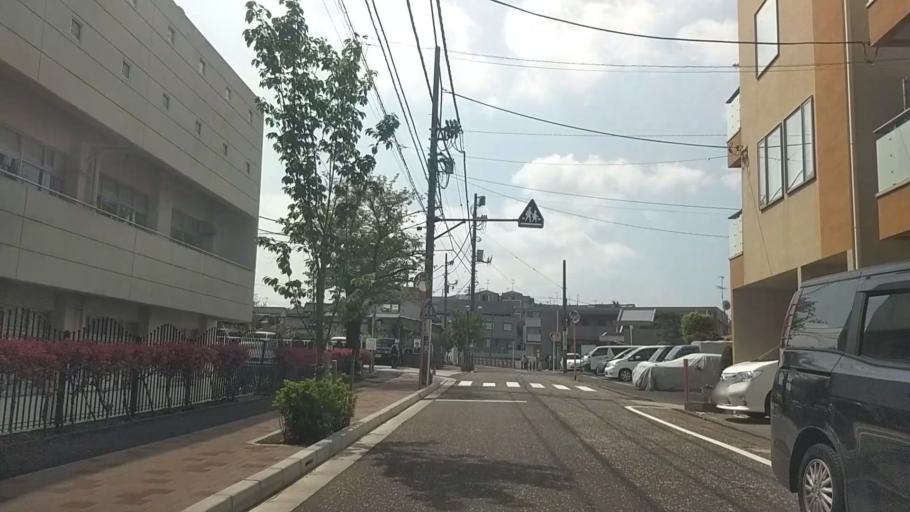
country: JP
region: Kanagawa
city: Yokohama
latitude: 35.3970
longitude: 139.5917
